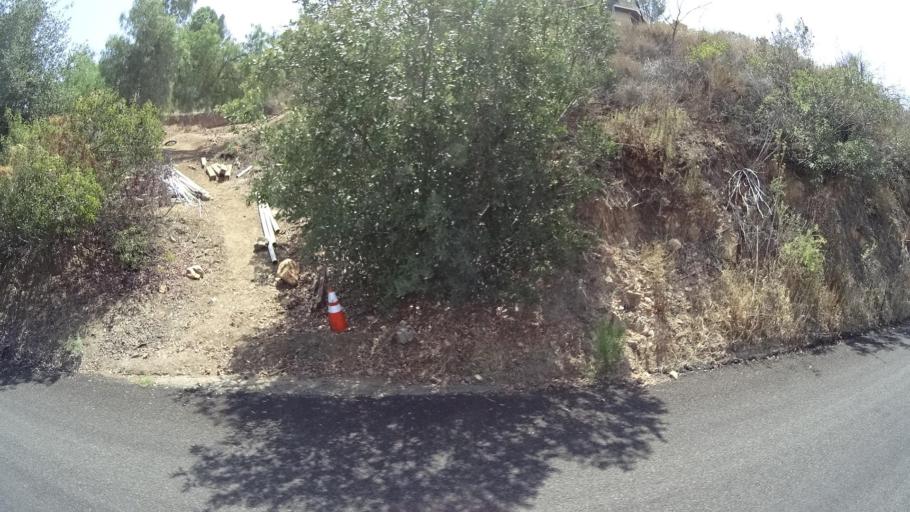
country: US
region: California
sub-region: San Diego County
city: Hidden Meadows
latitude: 33.1882
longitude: -117.0864
